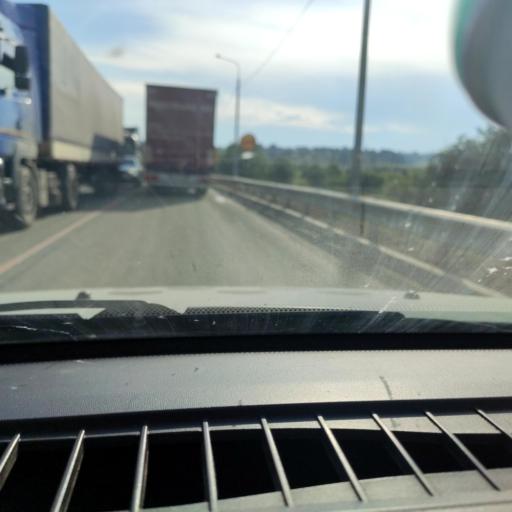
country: RU
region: Kirov
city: Kostino
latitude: 58.8531
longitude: 53.2255
